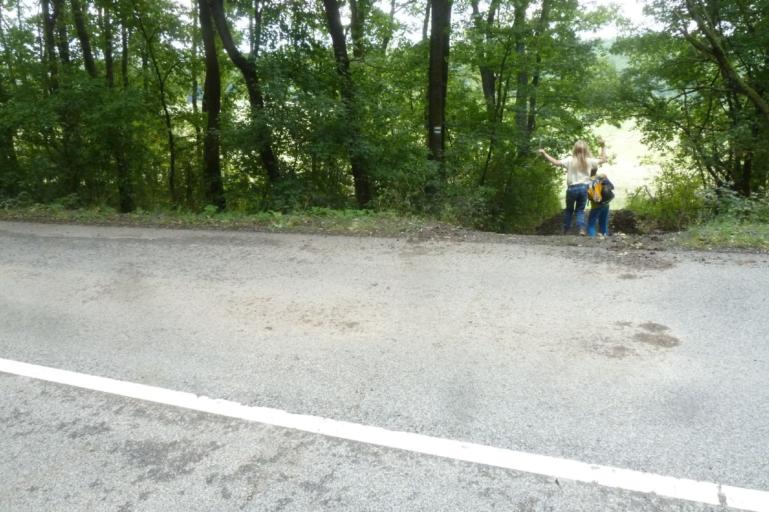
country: HU
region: Pest
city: Nagymaros
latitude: 47.8407
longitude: 18.9531
